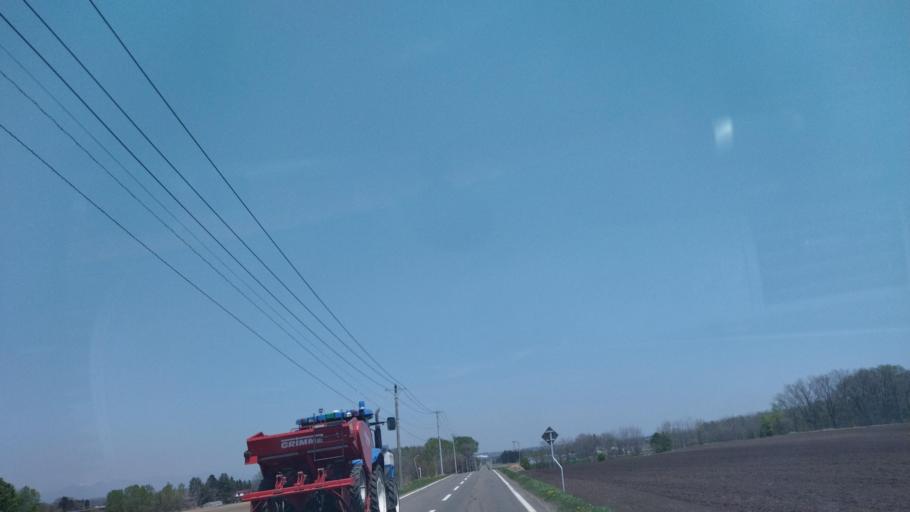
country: JP
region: Hokkaido
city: Obihiro
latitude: 42.8814
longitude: 143.0187
